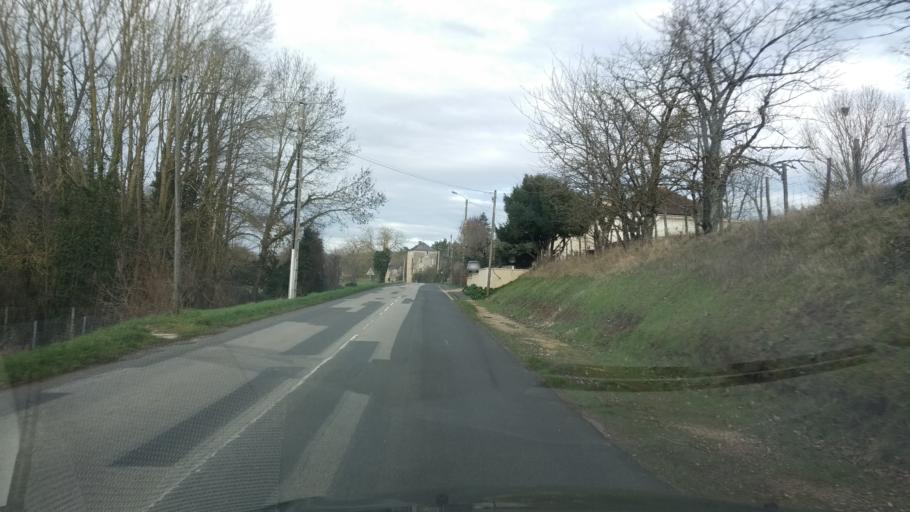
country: FR
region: Poitou-Charentes
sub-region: Departement de la Vienne
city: Chasseneuil-du-Poitou
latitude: 46.6482
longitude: 0.3867
